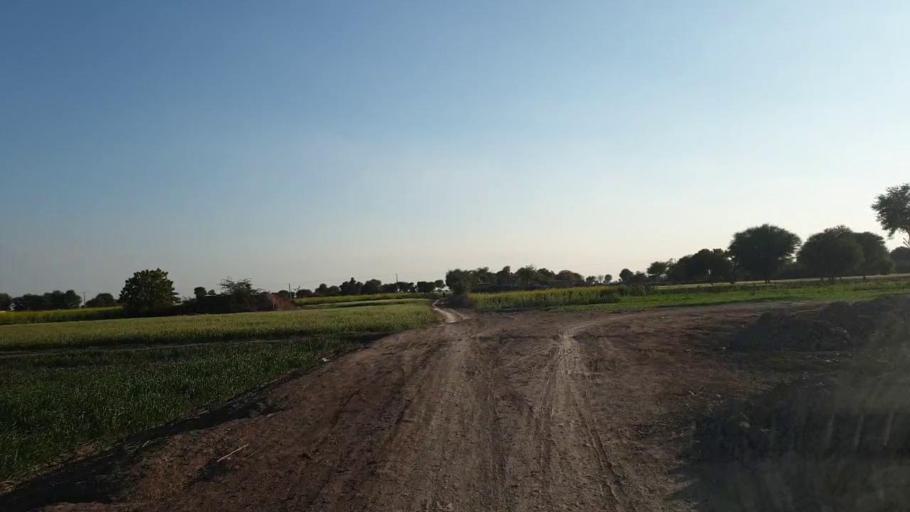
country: PK
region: Sindh
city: Shahpur Chakar
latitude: 26.1477
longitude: 68.5292
